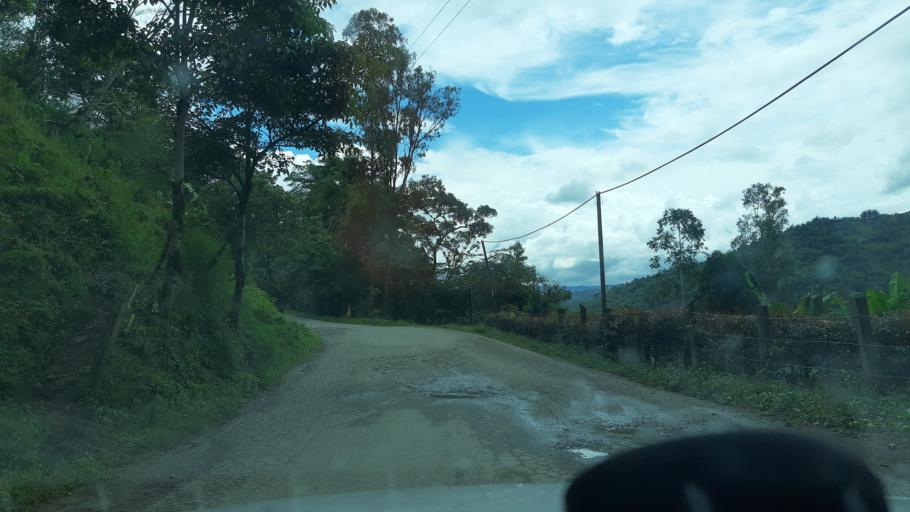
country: CO
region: Boyaca
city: Garagoa
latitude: 5.1130
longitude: -73.3641
